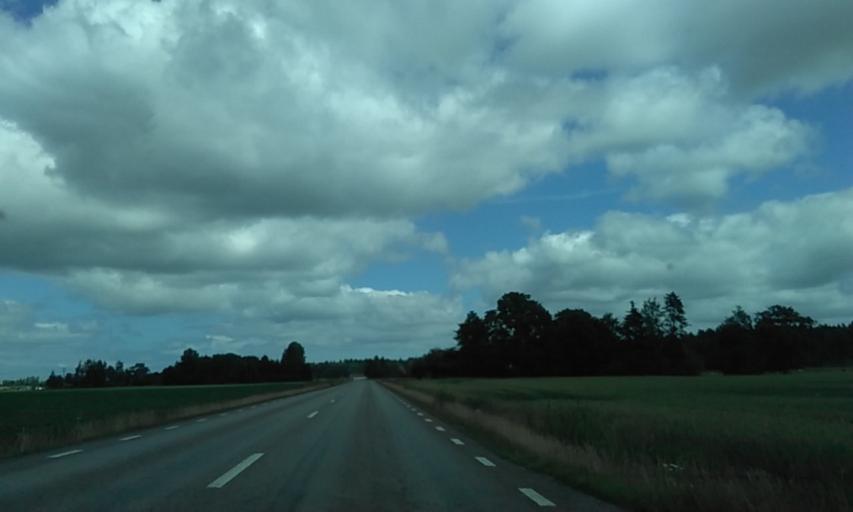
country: SE
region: Vaestra Goetaland
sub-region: Grastorps Kommun
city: Graestorp
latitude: 58.3136
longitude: 12.6713
